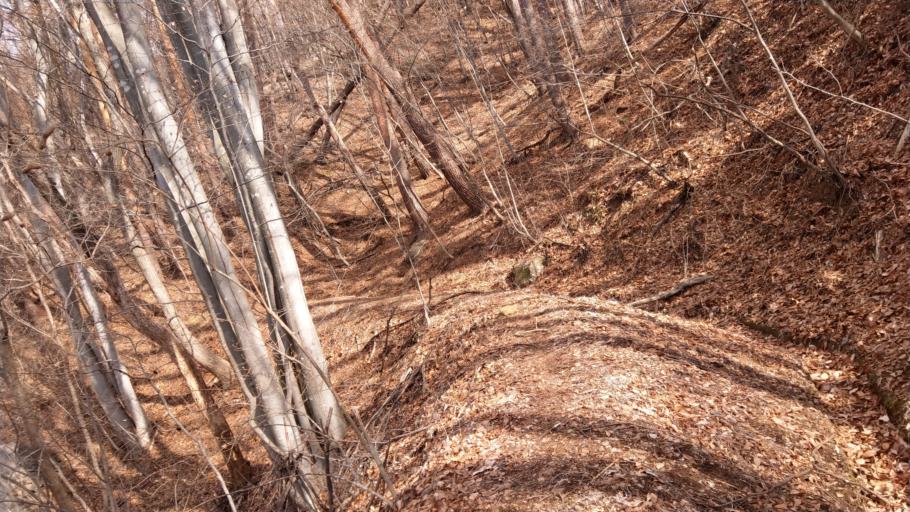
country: JP
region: Nagano
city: Komoro
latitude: 36.3568
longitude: 138.4203
